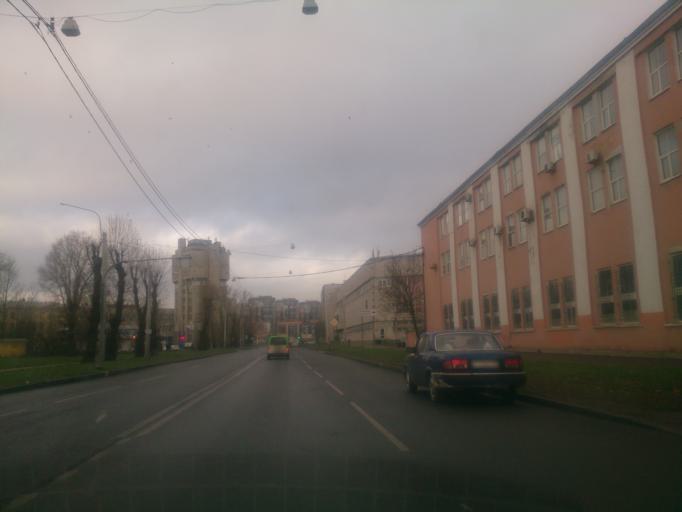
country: RU
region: St.-Petersburg
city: Admiralteisky
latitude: 59.8979
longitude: 30.2891
